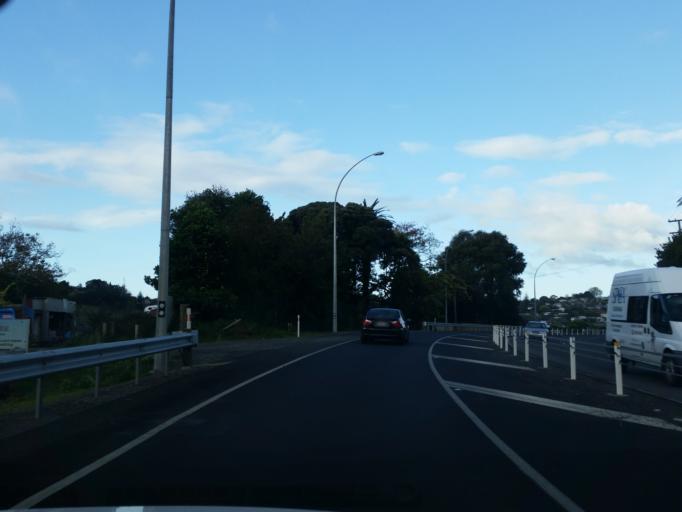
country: NZ
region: Bay of Plenty
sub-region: Tauranga City
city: Tauranga
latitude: -37.6937
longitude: 176.1210
